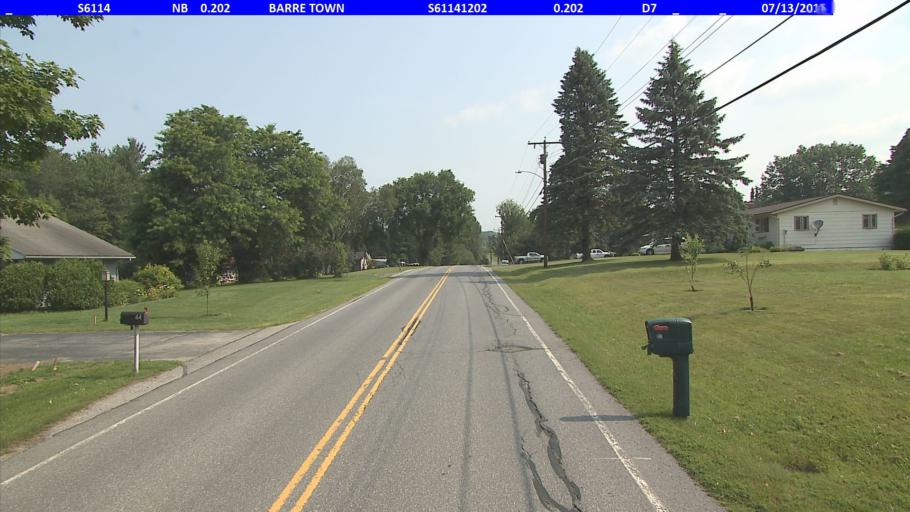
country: US
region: Vermont
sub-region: Washington County
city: Barre
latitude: 44.1947
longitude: -72.4795
